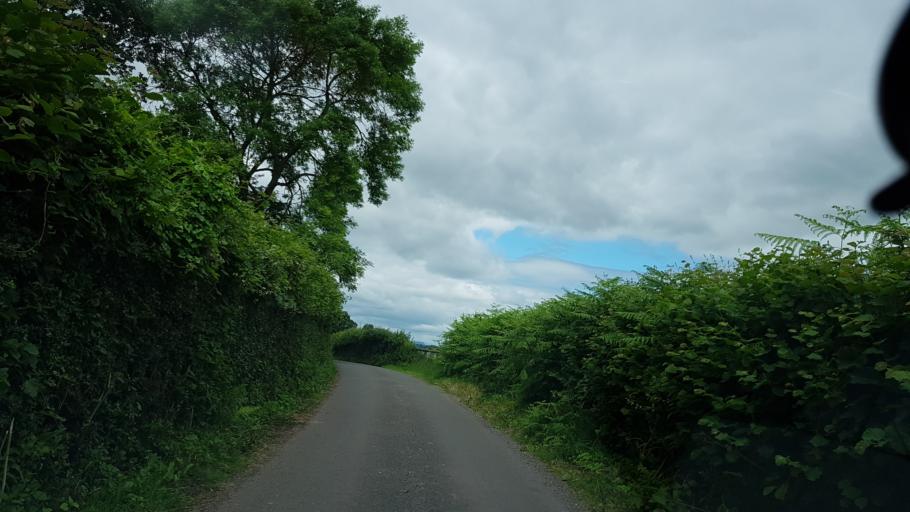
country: GB
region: Wales
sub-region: Monmouthshire
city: Llanarth
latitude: 51.8062
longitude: -2.8413
